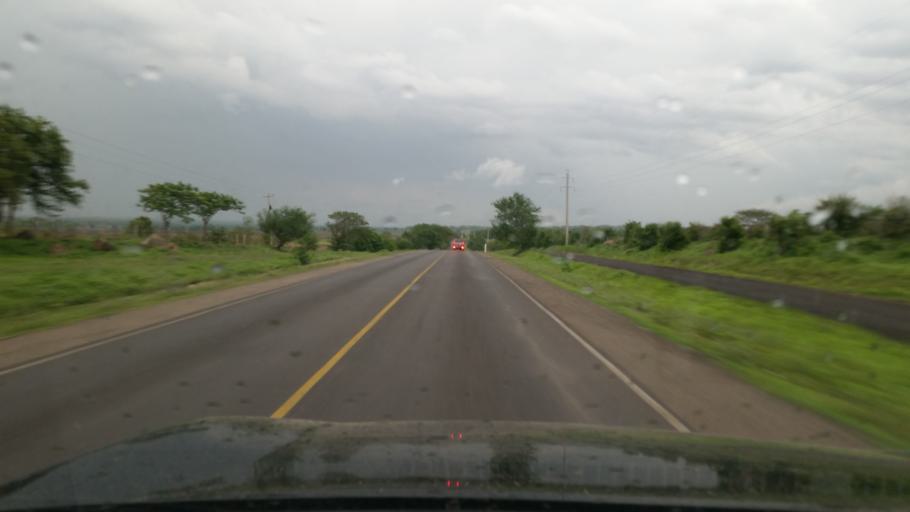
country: NI
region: Chinandega
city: Puerto Morazan
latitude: 12.7912
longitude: -87.0126
